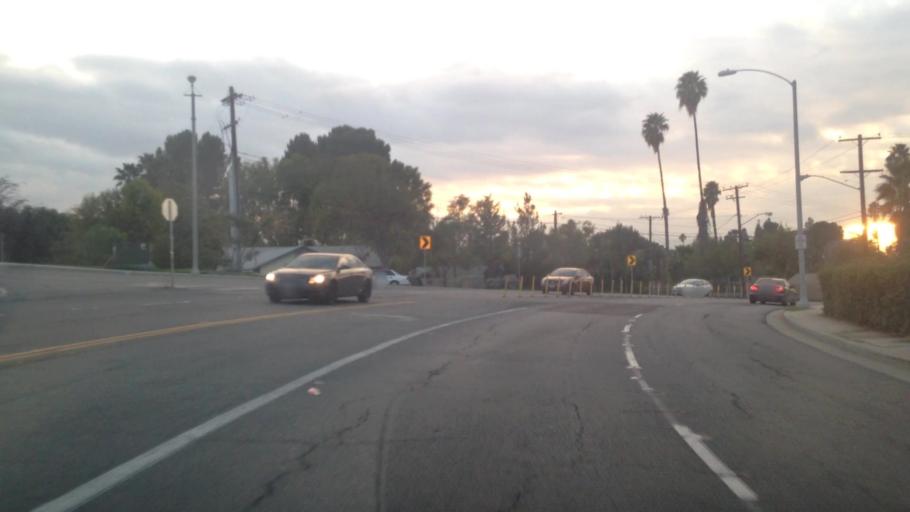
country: US
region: California
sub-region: Riverside County
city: Riverside
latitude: 33.9614
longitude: -117.3845
